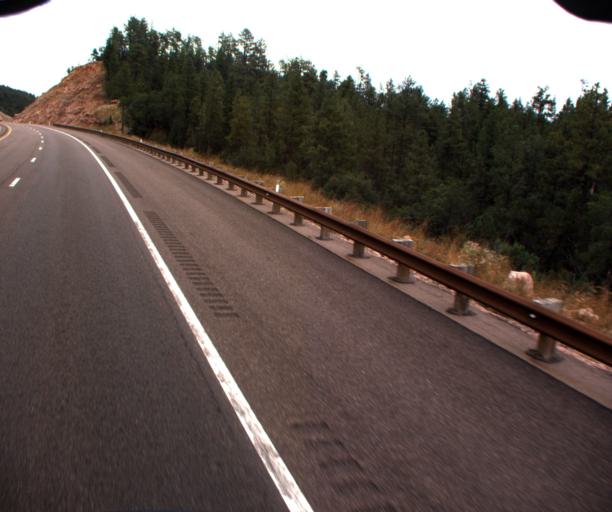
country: US
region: Arizona
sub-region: Gila County
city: Star Valley
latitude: 34.3235
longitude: -111.0788
